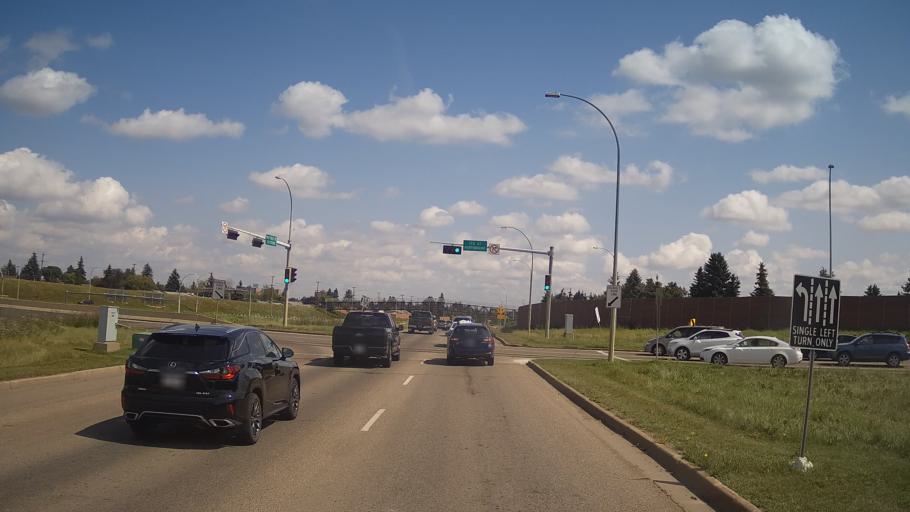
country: CA
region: Alberta
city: St. Albert
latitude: 53.5115
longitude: -113.6151
